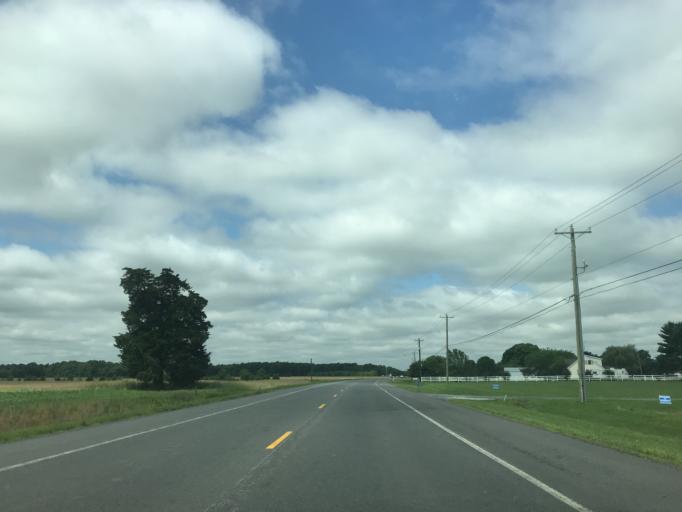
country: US
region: Maryland
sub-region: Caroline County
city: Ridgely
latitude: 38.9296
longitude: -75.9118
